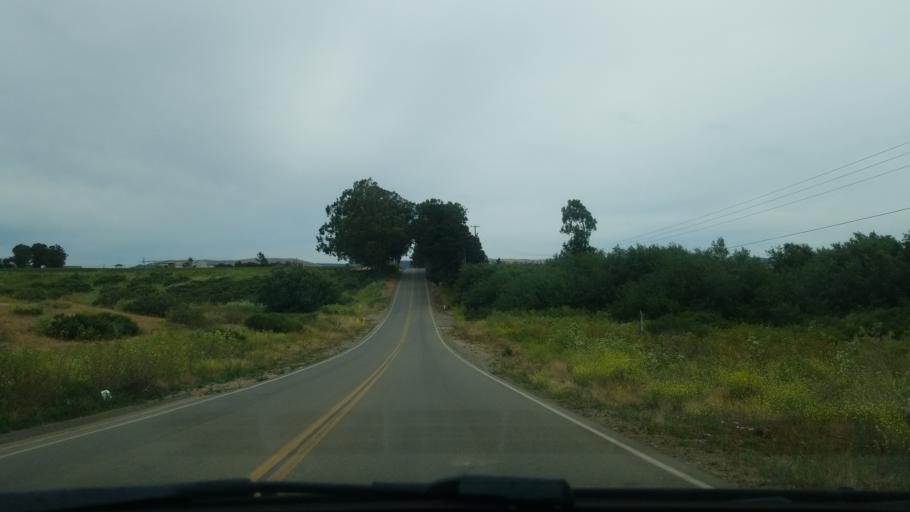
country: US
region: California
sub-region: Santa Barbara County
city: Santa Maria
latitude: 34.9159
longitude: -120.4902
